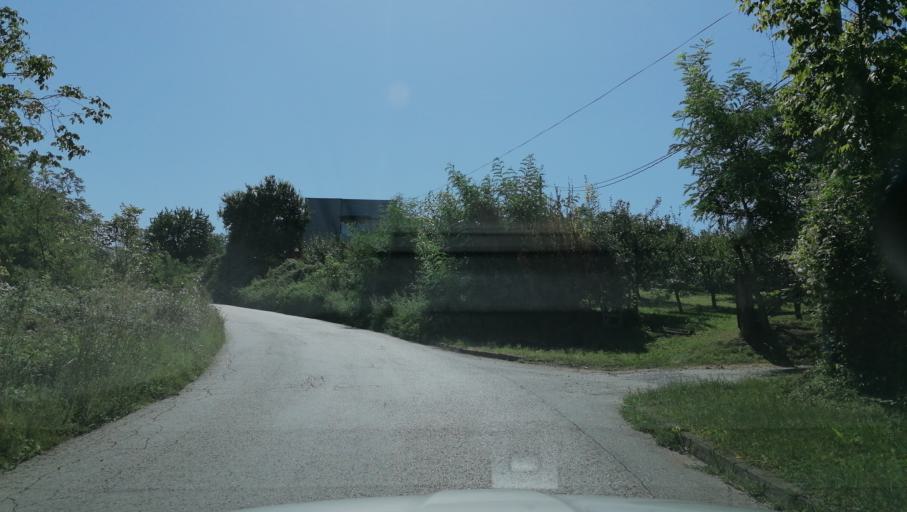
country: RS
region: Central Serbia
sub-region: Kolubarski Okrug
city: Valjevo
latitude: 44.2537
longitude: 19.8755
